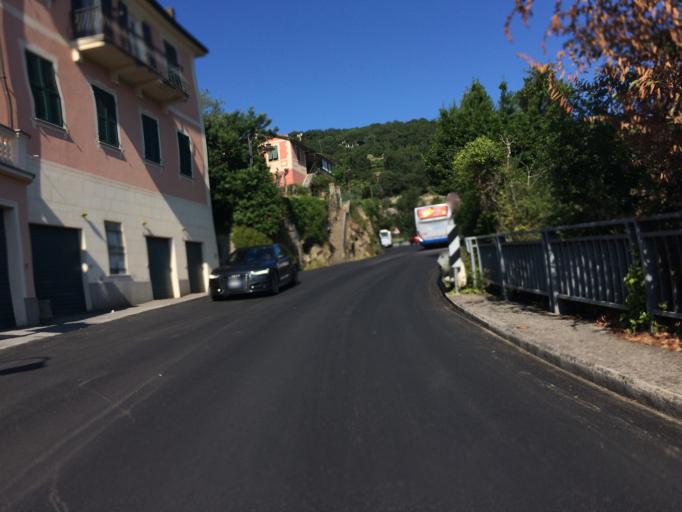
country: IT
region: Liguria
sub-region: Provincia di Genova
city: Santa Margherita Ligure
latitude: 44.3391
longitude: 9.1856
